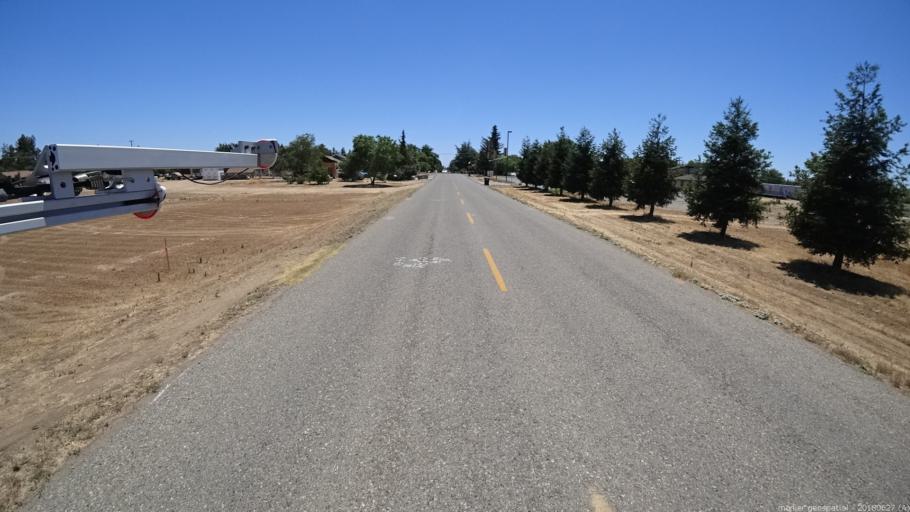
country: US
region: California
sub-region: Madera County
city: Bonadelle Ranchos-Madera Ranchos
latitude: 36.9295
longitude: -119.8761
